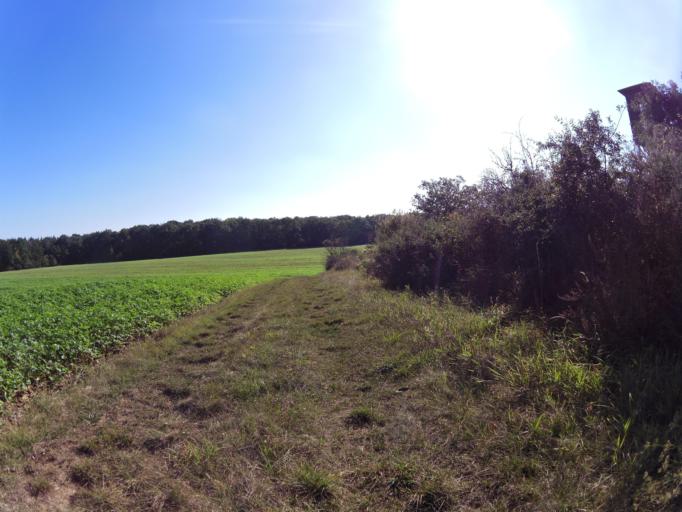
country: DE
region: Bavaria
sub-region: Regierungsbezirk Unterfranken
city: Sommerhausen
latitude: 49.6849
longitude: 10.0411
